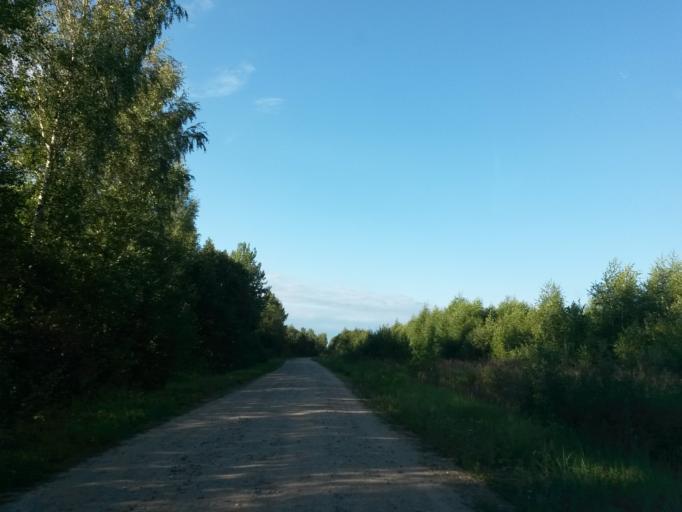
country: RU
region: Jaroslavl
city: Tutayev
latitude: 57.9420
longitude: 39.4472
